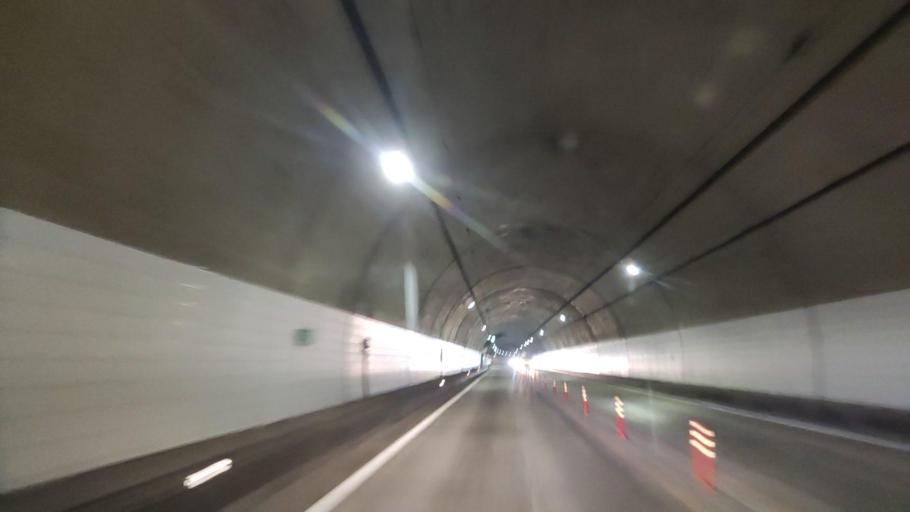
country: JP
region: Akita
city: Odate
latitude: 40.3640
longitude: 140.6967
